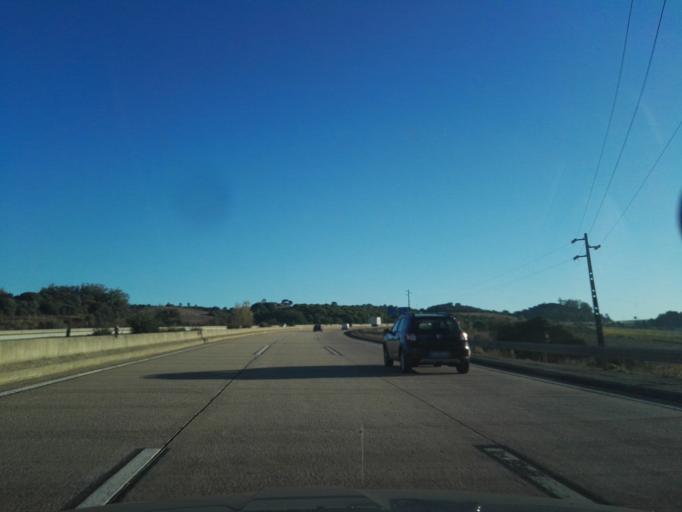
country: PT
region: Lisbon
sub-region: Loures
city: Bucelas
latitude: 38.9044
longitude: -9.0901
